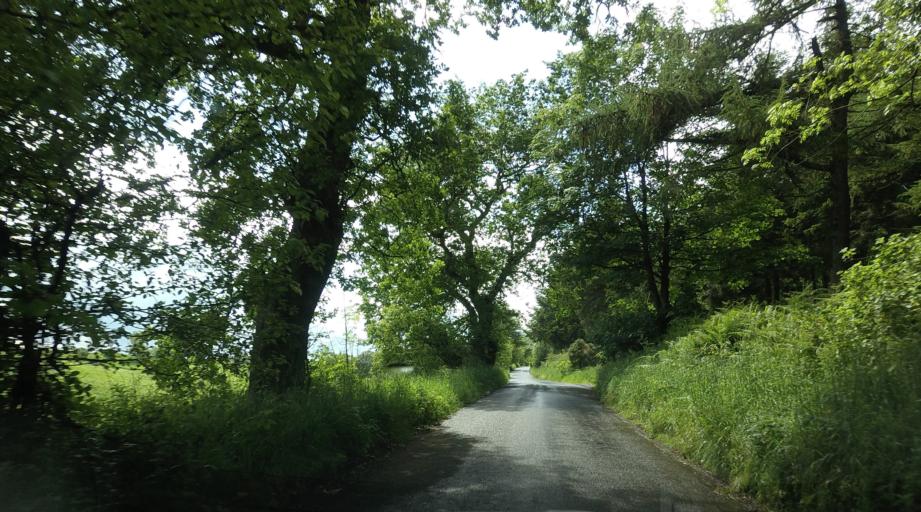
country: GB
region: Scotland
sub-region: Fife
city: Ballingry
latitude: 56.1629
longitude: -3.3394
